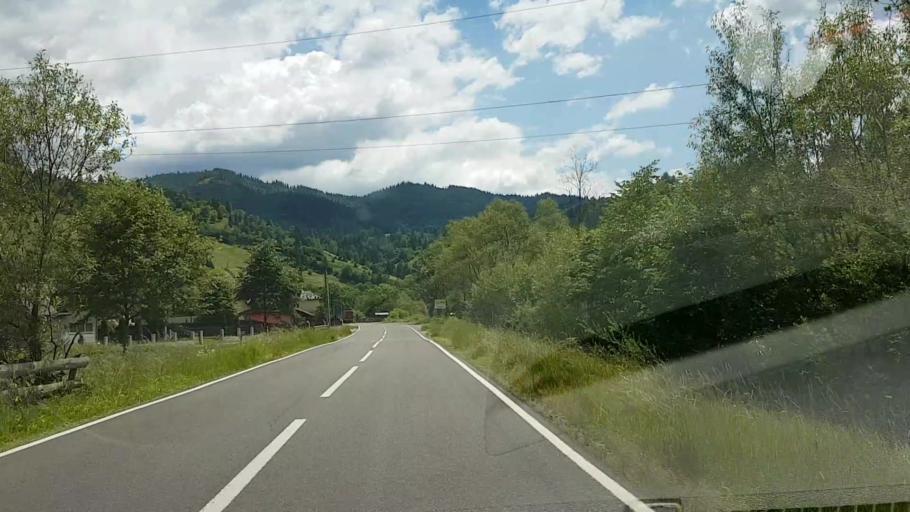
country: RO
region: Suceava
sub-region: Comuna Crucea
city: Crucea
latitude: 47.3928
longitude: 25.5726
